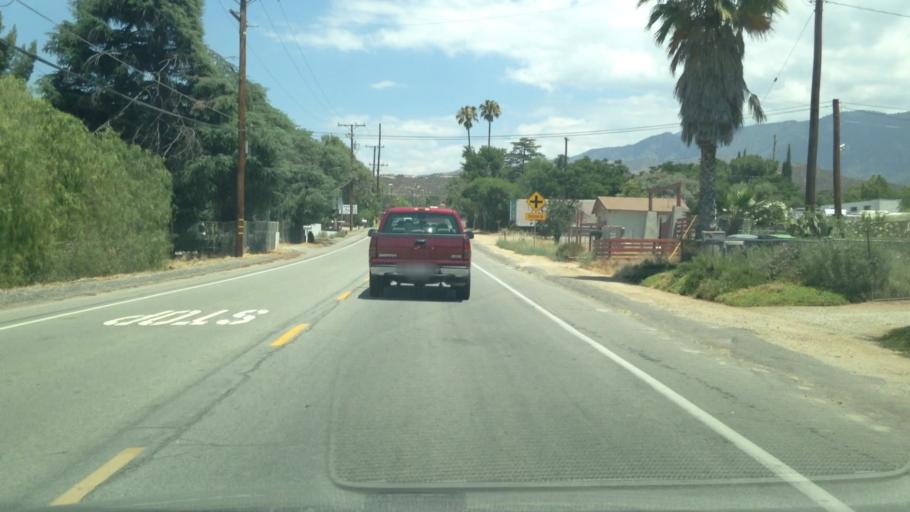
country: US
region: California
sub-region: Riverside County
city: Cherry Valley
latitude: 33.9742
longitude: -116.9773
